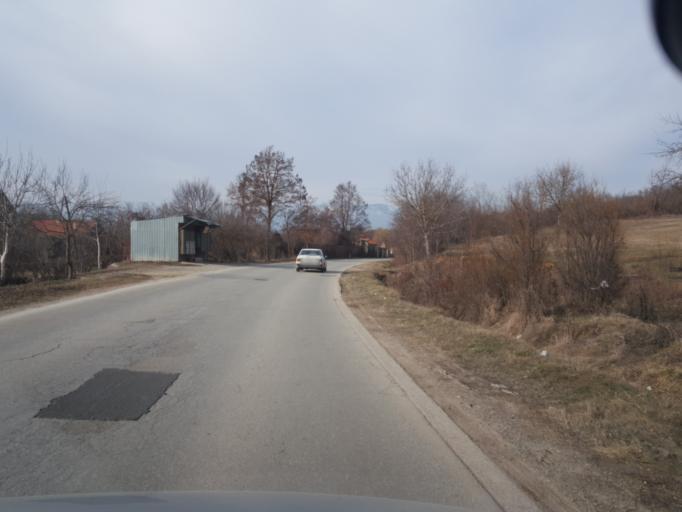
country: XK
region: Pec
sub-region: Komuna e Klines
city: Klina
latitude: 42.6692
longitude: 20.5352
